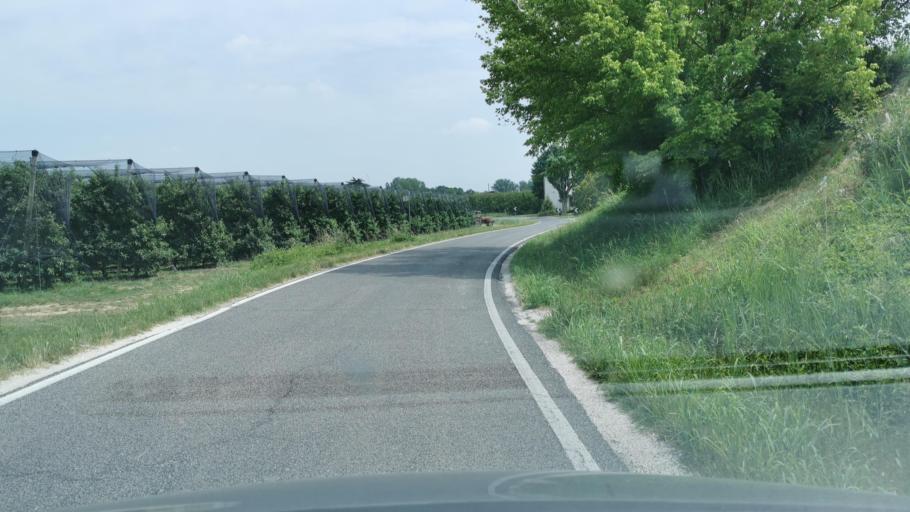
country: IT
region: Emilia-Romagna
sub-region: Provincia di Ravenna
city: Russi
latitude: 44.3848
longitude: 12.0020
